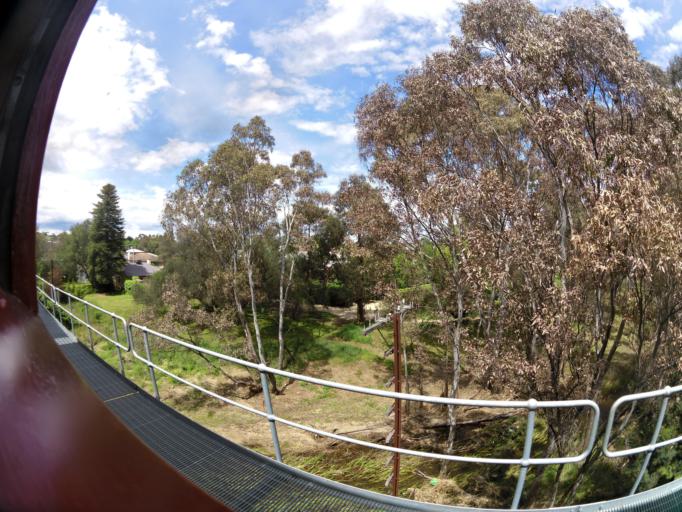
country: AU
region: Victoria
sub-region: Mount Alexander
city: Castlemaine
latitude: -37.0686
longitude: 144.2147
